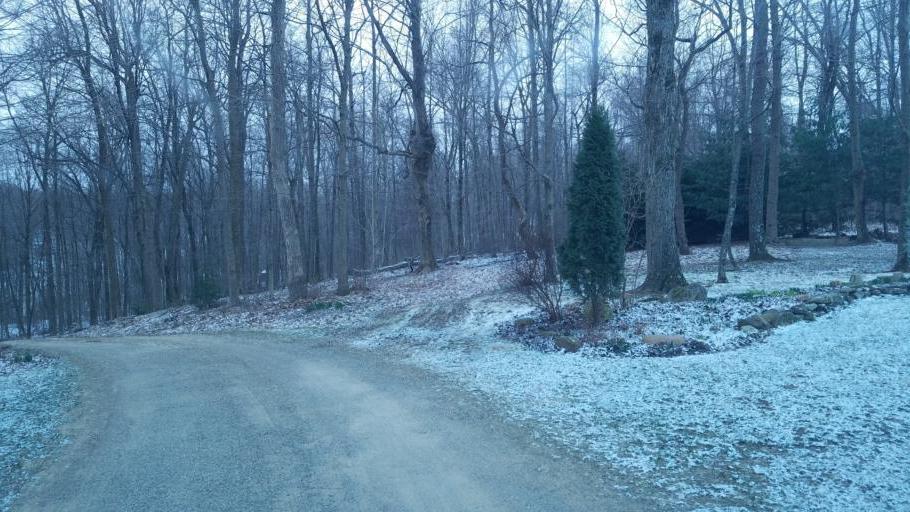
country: US
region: Ohio
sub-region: Knox County
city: Danville
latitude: 40.5207
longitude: -82.3628
